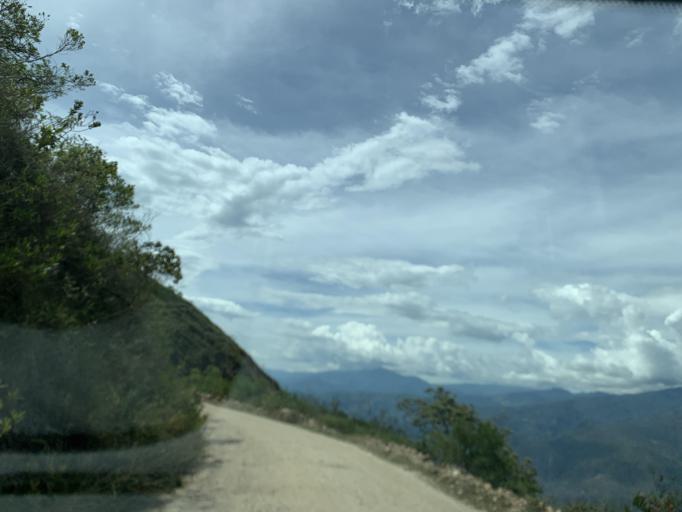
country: CO
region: Boyaca
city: Tipacoque
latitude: 6.4478
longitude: -72.7064
